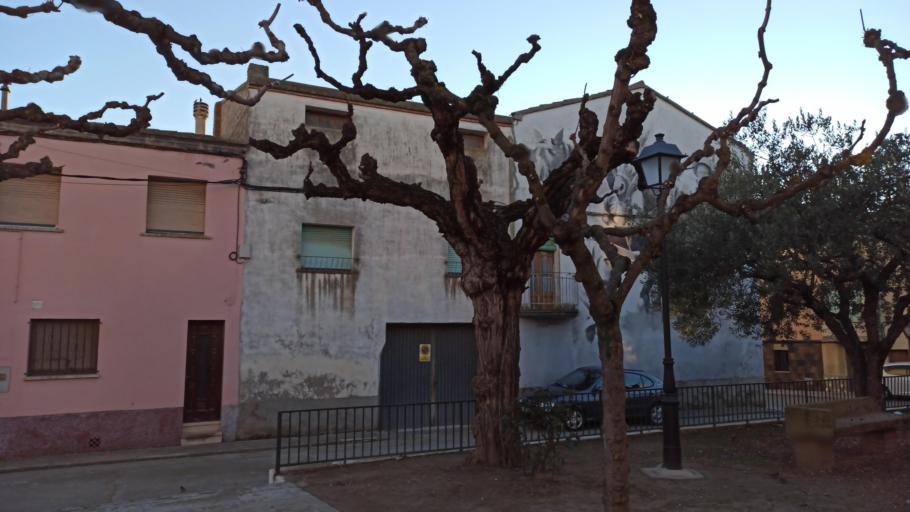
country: ES
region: Catalonia
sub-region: Provincia de Lleida
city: Penelles
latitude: 41.7581
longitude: 0.9653
